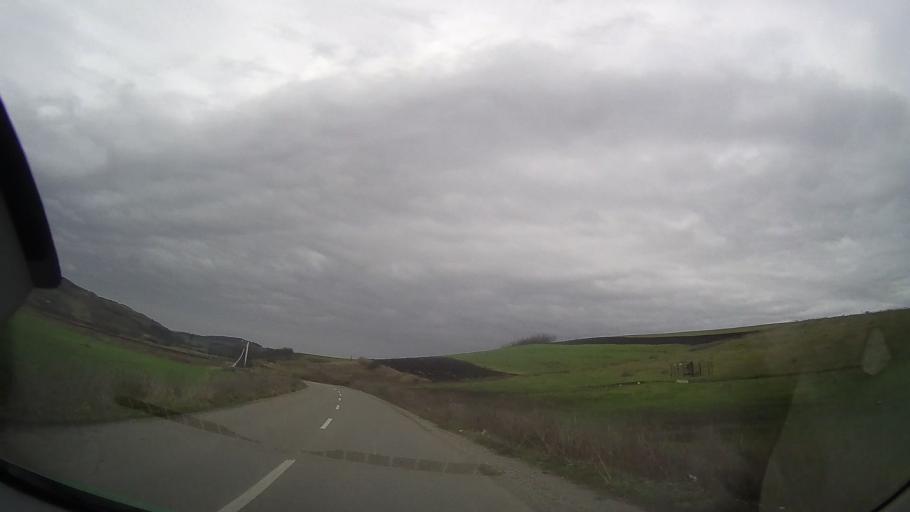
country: RO
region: Mures
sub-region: Comuna Craesti
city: Craiesti
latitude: 46.7772
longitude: 24.4255
